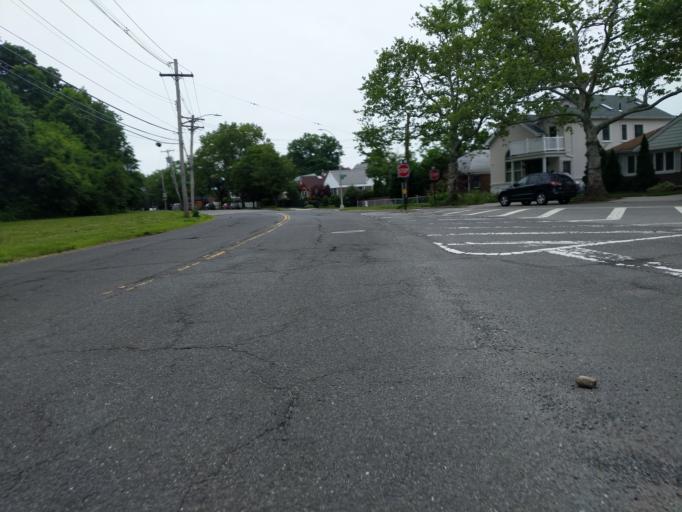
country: US
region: New York
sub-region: Queens County
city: Jamaica
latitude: 40.7440
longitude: -73.7948
